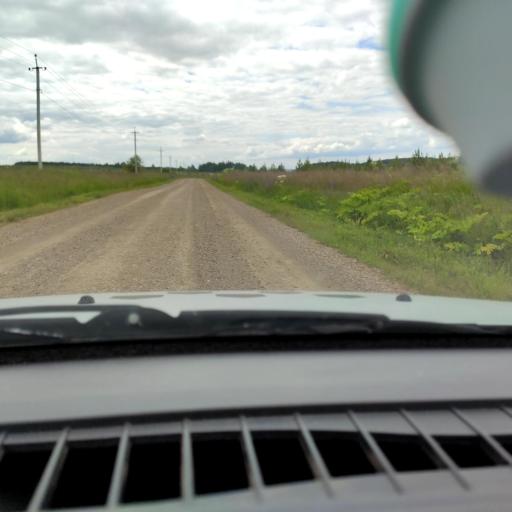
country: RU
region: Perm
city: Suksun
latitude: 57.1911
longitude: 57.5601
